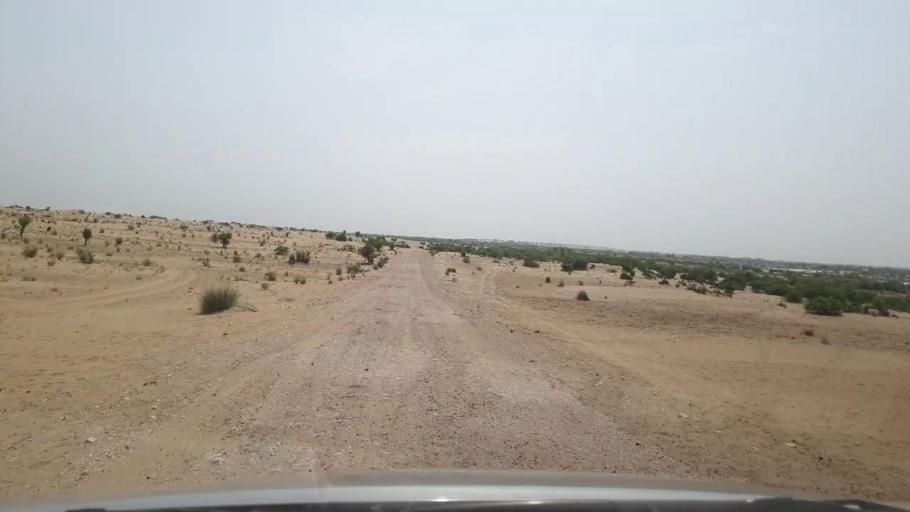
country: PK
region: Sindh
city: Rohri
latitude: 27.6176
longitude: 69.1193
